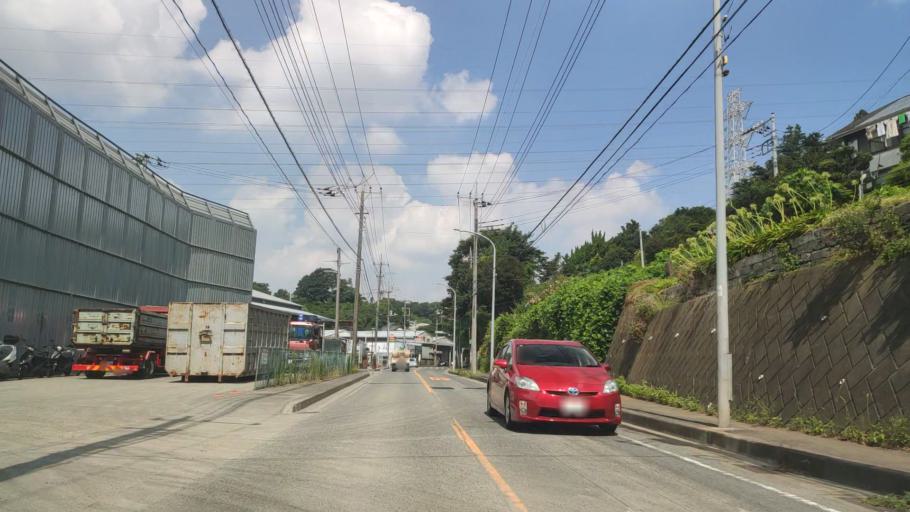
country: JP
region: Kanagawa
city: Minami-rinkan
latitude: 35.4385
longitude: 139.5089
